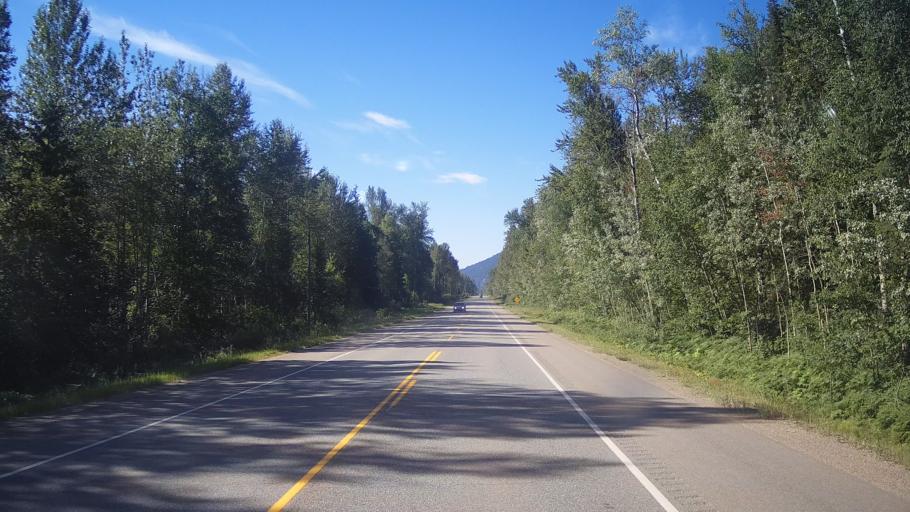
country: CA
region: British Columbia
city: Chase
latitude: 51.5302
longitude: -120.1701
